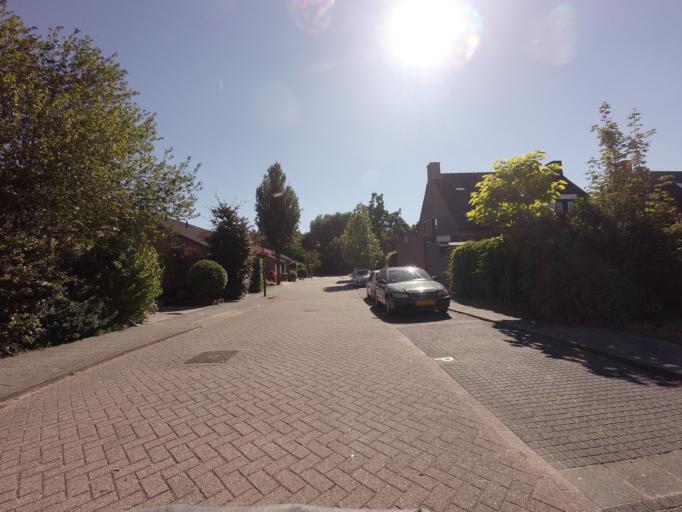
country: NL
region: Utrecht
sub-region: Stichtse Vecht
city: Spechtenkamp
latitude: 52.1362
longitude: 5.0127
